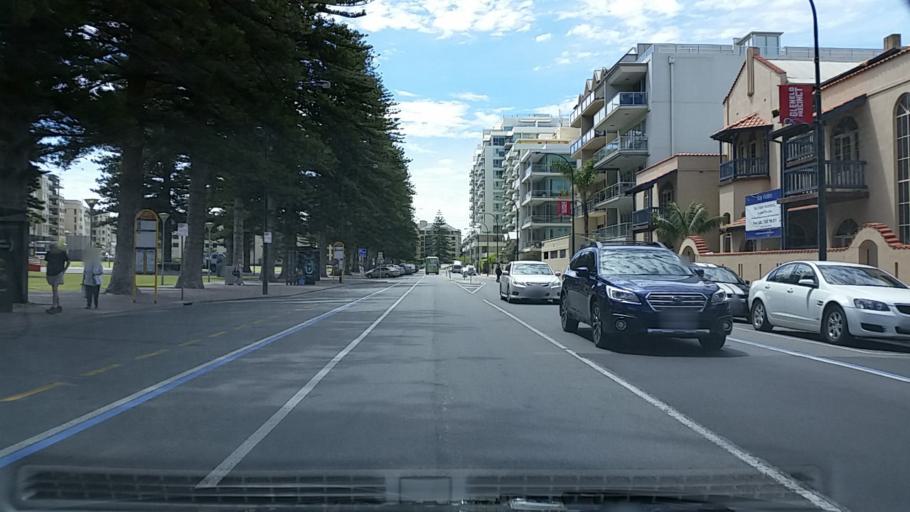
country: AU
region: South Australia
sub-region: Adelaide
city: Glenelg
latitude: -34.9794
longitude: 138.5124
